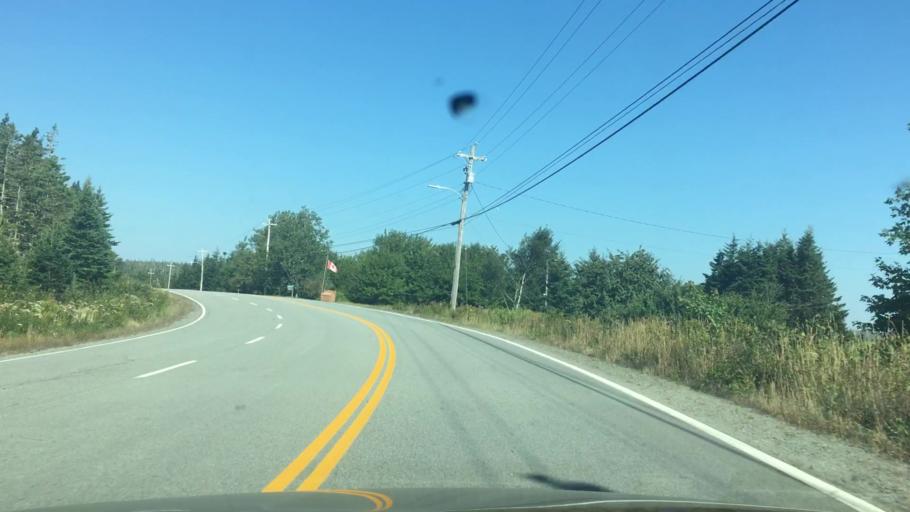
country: CA
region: Nova Scotia
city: New Glasgow
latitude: 44.8156
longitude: -62.6313
